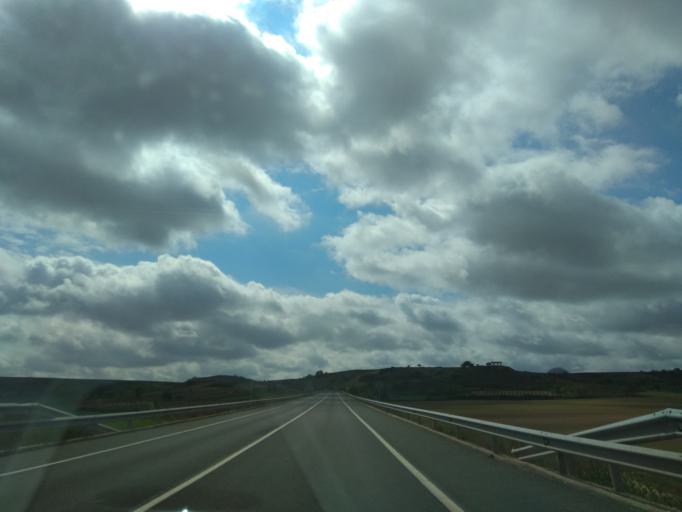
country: ES
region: La Rioja
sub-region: Provincia de La Rioja
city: Casalarreina
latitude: 42.5497
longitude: -2.8924
